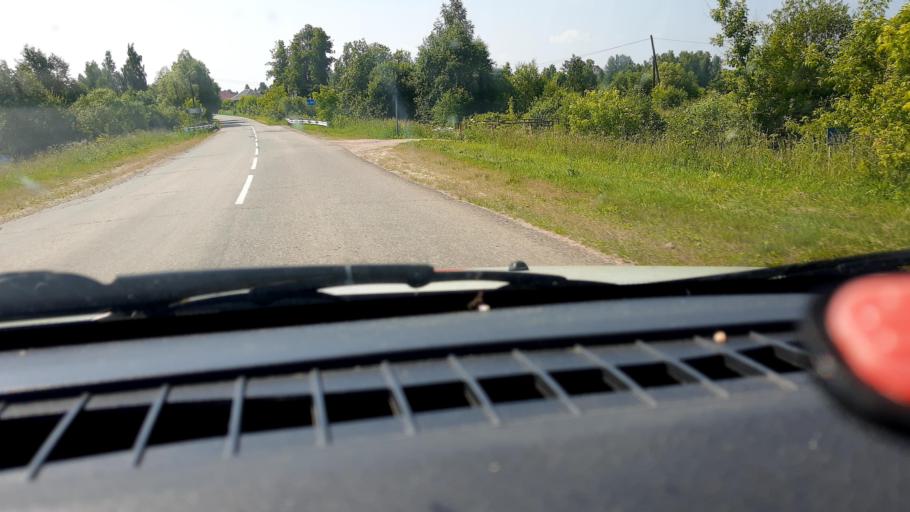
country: RU
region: Nizjnij Novgorod
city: Sharanga
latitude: 57.0543
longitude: 46.5452
